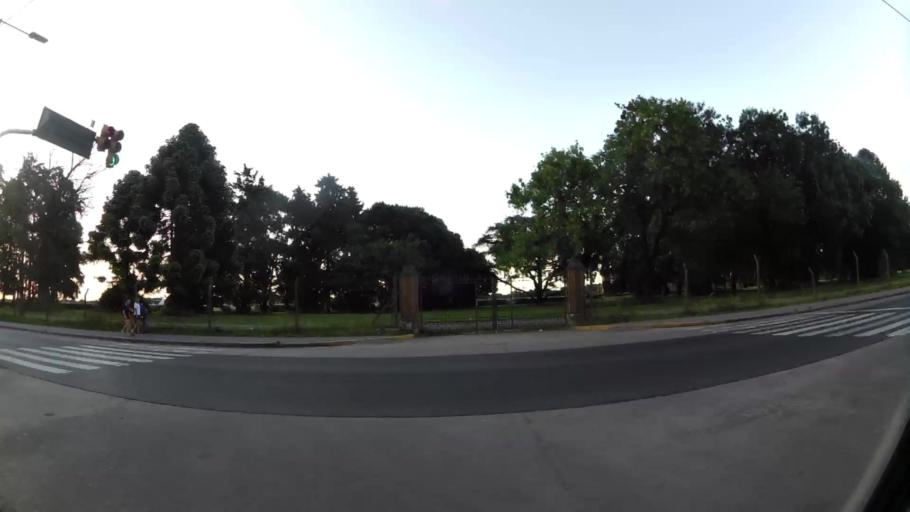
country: AR
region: Buenos Aires
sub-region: Partido de San Isidro
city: San Isidro
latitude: -34.4832
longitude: -58.5127
